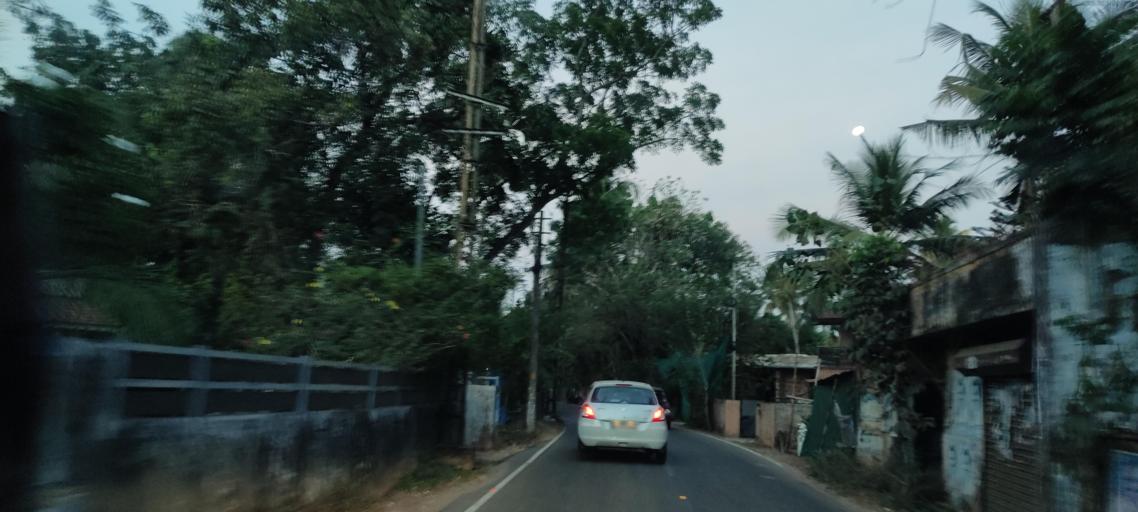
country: IN
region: Kerala
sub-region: Alappuzha
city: Kutiatodu
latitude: 9.7695
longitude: 76.3248
